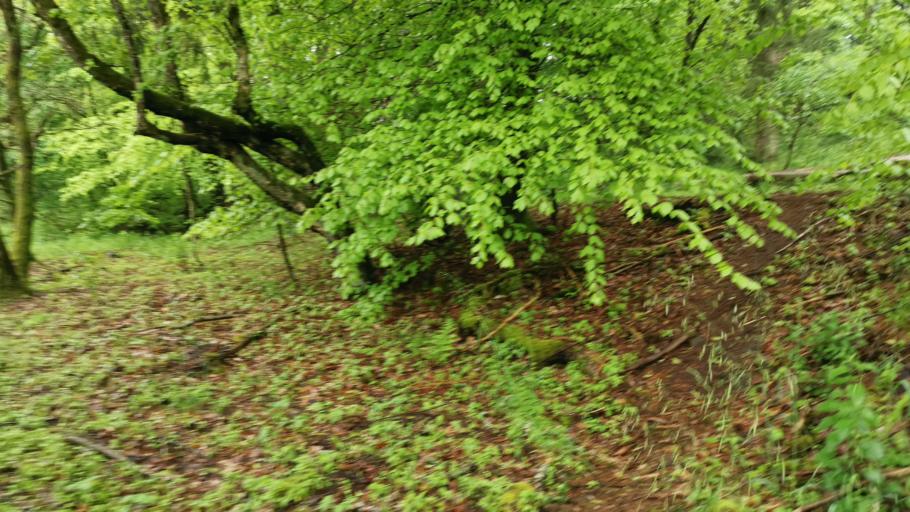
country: DE
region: Saarland
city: Kirkel
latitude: 49.2666
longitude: 7.1873
